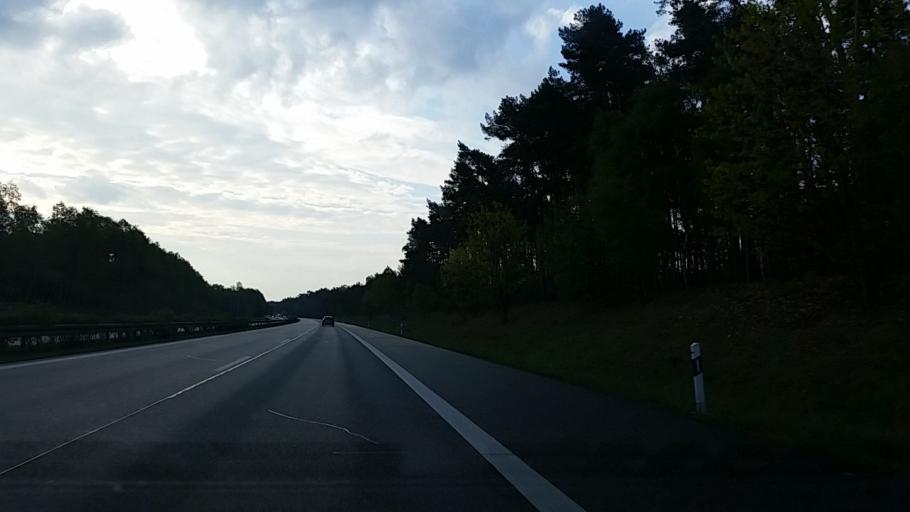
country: DE
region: Mecklenburg-Vorpommern
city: Neustadt-Glewe
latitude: 53.3772
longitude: 11.6279
